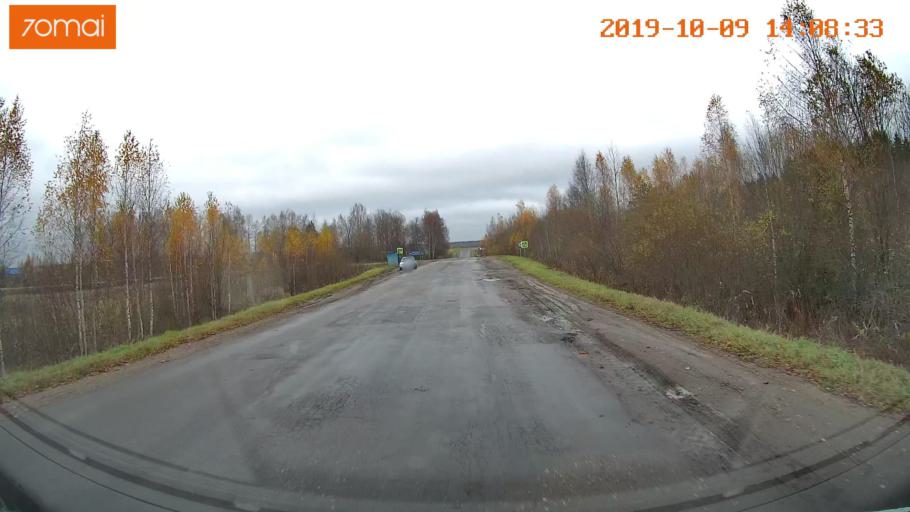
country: RU
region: Kostroma
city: Buy
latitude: 58.4775
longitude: 41.4375
